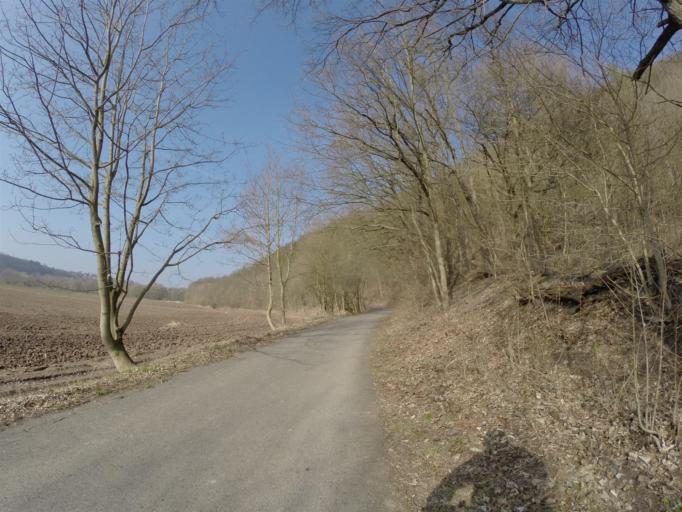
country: DE
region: Thuringia
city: Golmsdorf
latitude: 50.9875
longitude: 11.6746
